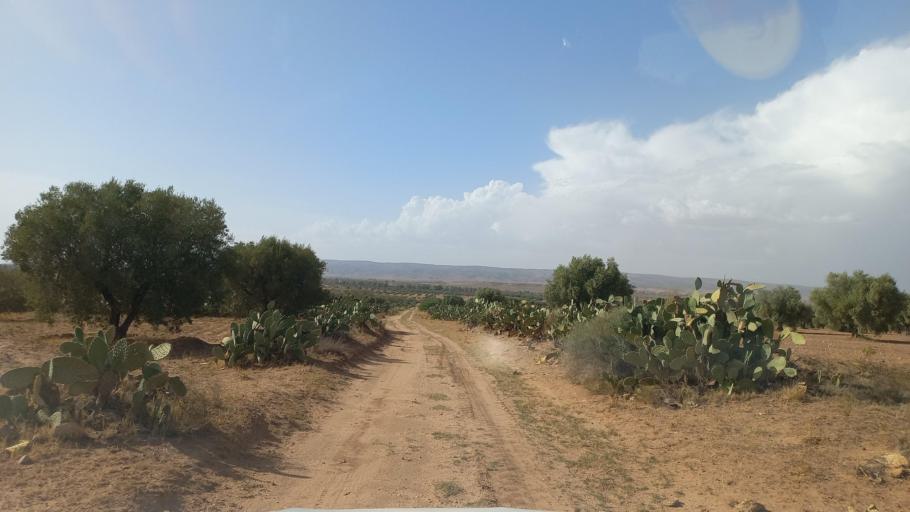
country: TN
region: Al Qasrayn
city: Kasserine
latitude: 35.2129
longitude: 8.9520
